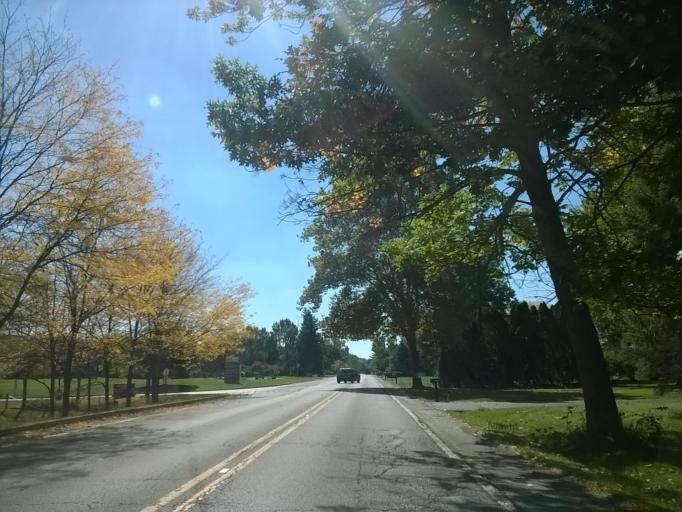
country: US
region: Indiana
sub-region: Marion County
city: Meridian Hills
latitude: 39.8797
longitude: -86.1745
